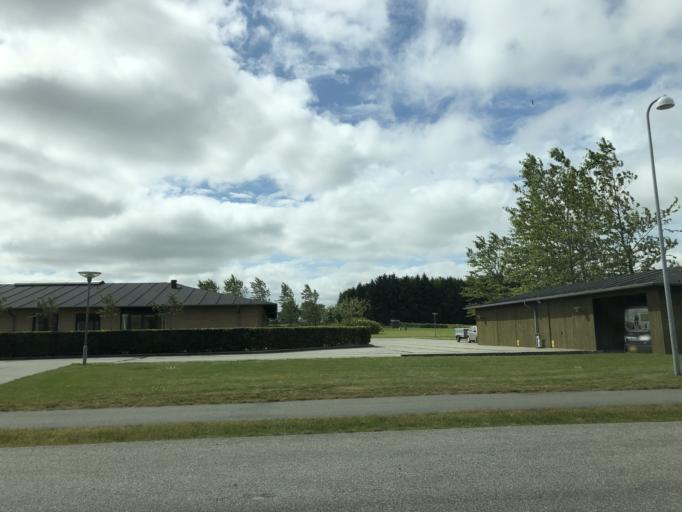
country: DK
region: Central Jutland
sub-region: Herning Kommune
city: Vildbjerg
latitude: 56.1877
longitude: 8.7466
